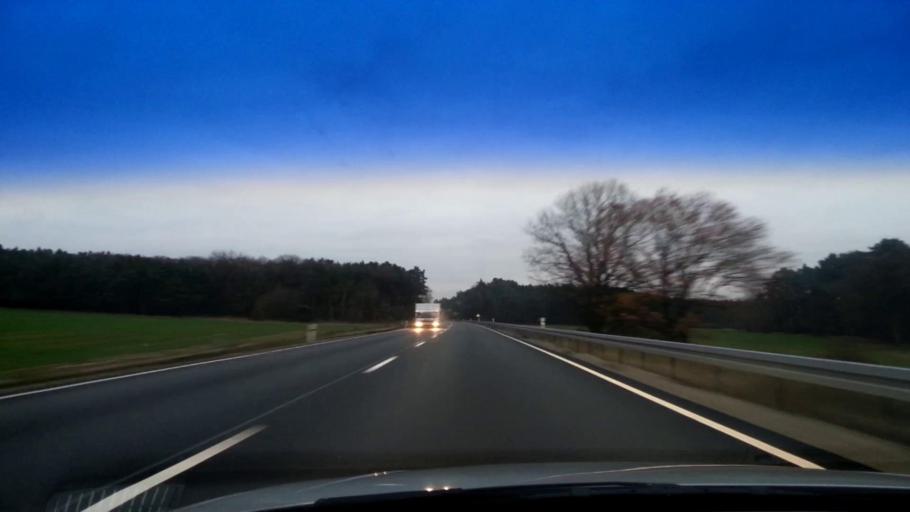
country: DE
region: Bavaria
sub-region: Upper Franconia
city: Pettstadt
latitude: 49.7839
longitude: 10.9189
